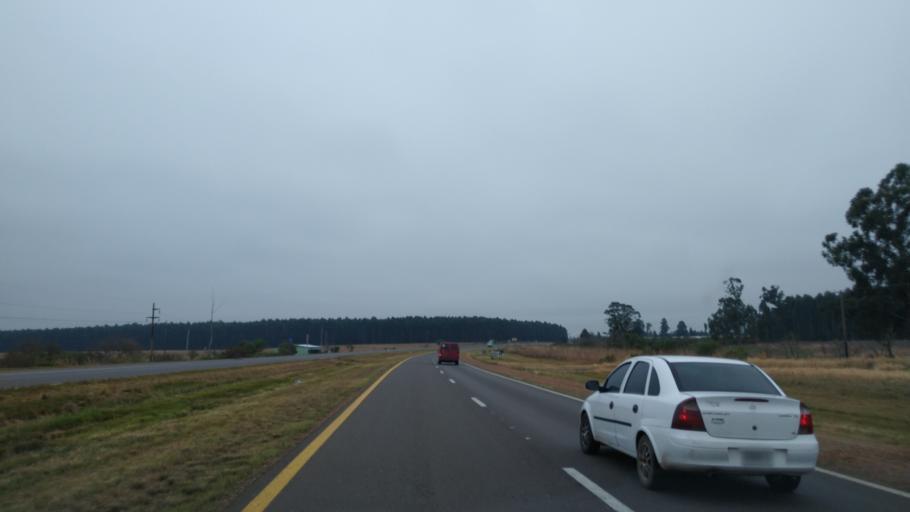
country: AR
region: Entre Rios
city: Chajari
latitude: -30.8349
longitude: -58.0493
